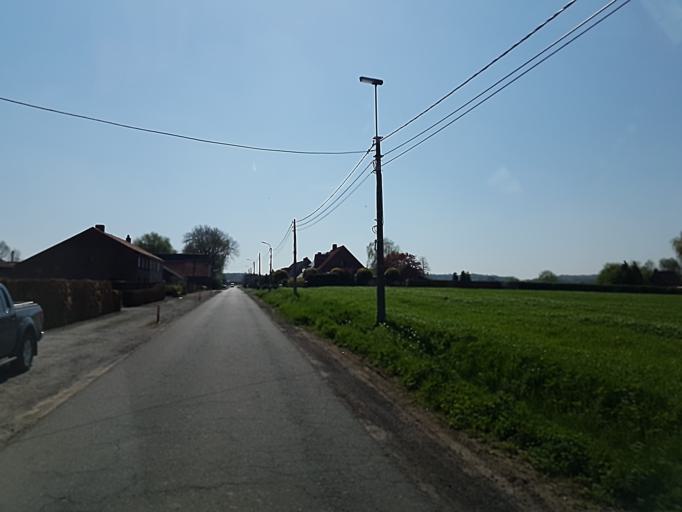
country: BE
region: Flanders
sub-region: Provincie West-Vlaanderen
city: Zonnebeke
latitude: 50.8601
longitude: 2.9569
